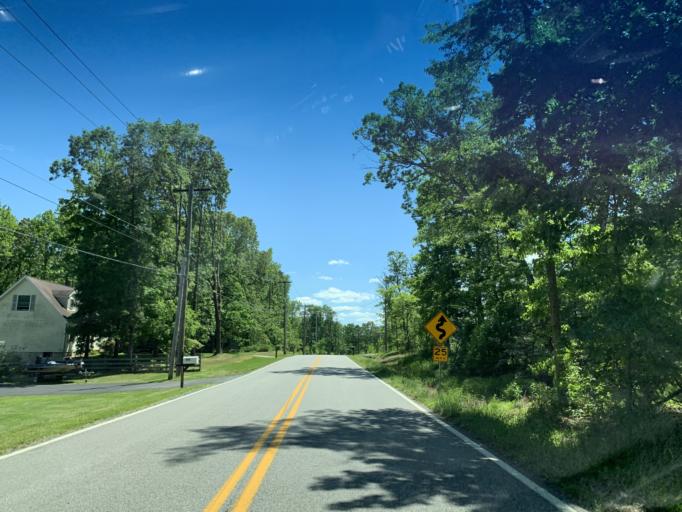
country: US
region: Maryland
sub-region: Cecil County
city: Charlestown
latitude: 39.5233
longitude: -75.9396
